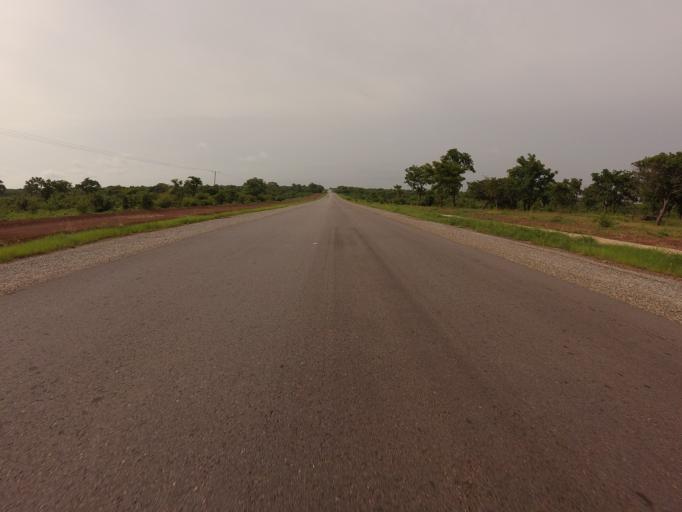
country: GH
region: Northern
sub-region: Yendi
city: Yendi
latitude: 9.6296
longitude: -0.0577
